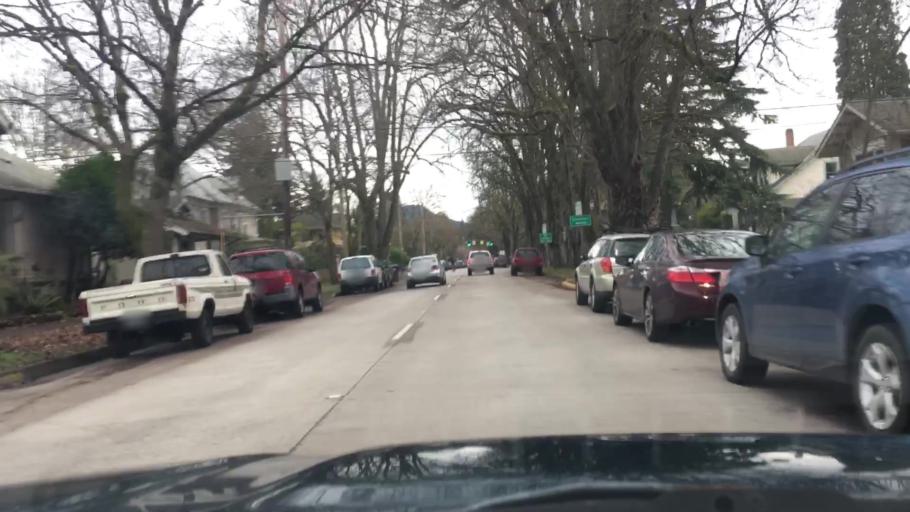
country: US
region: Oregon
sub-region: Lane County
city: Eugene
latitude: 44.0497
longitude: -123.1019
